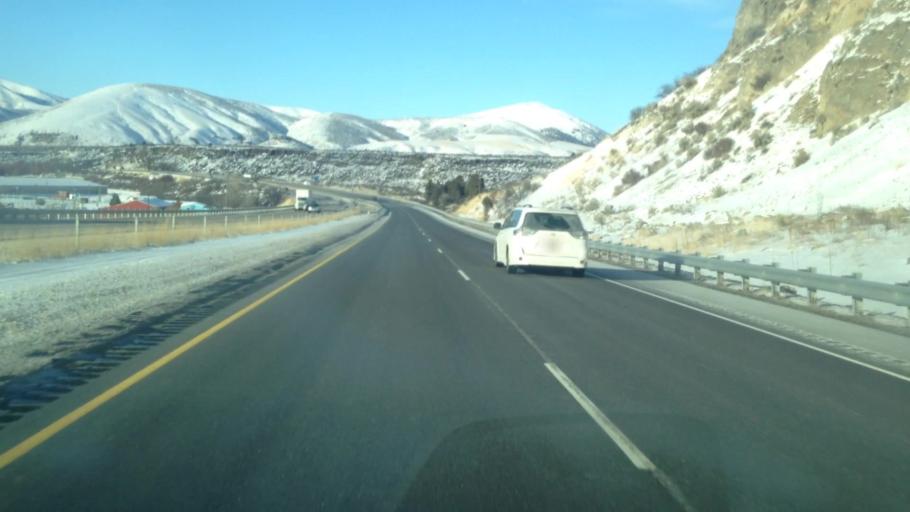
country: US
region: Idaho
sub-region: Bannock County
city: Pocatello
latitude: 42.7796
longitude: -112.2302
